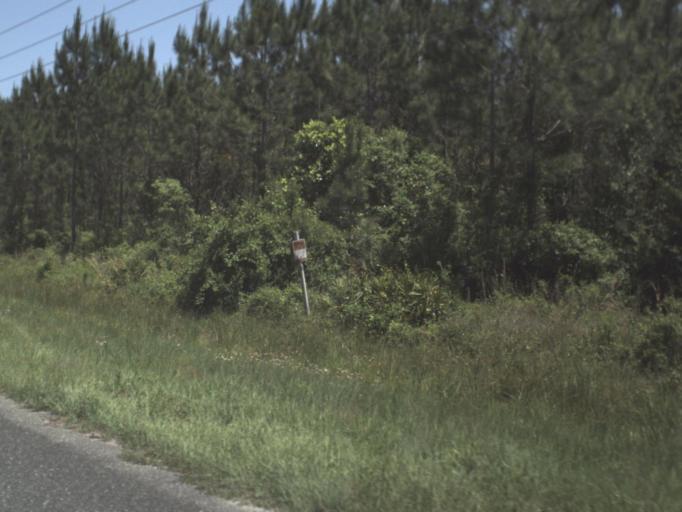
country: US
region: Florida
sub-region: Union County
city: Lake Butler
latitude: 30.2068
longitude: -82.4077
